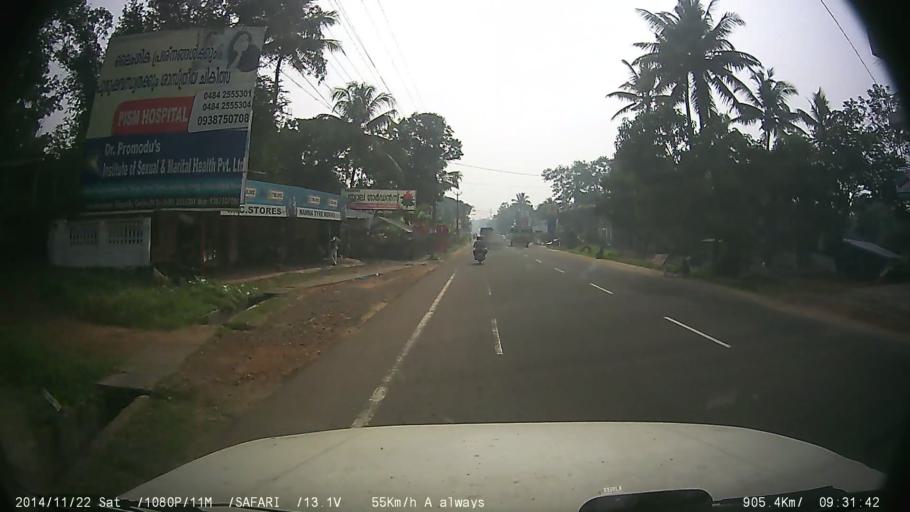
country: IN
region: Kerala
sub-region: Ernakulam
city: Angamali
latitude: 10.1808
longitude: 76.4140
